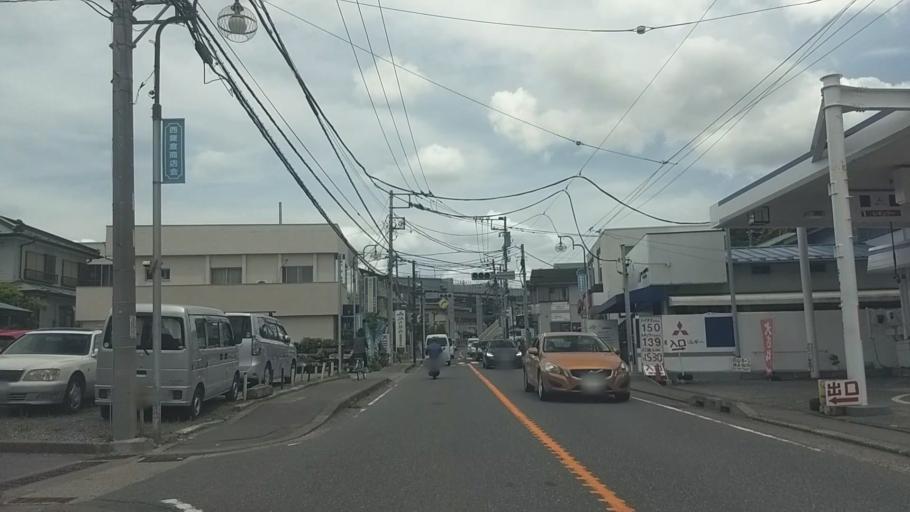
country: JP
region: Kanagawa
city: Fujisawa
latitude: 35.3178
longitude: 139.5033
